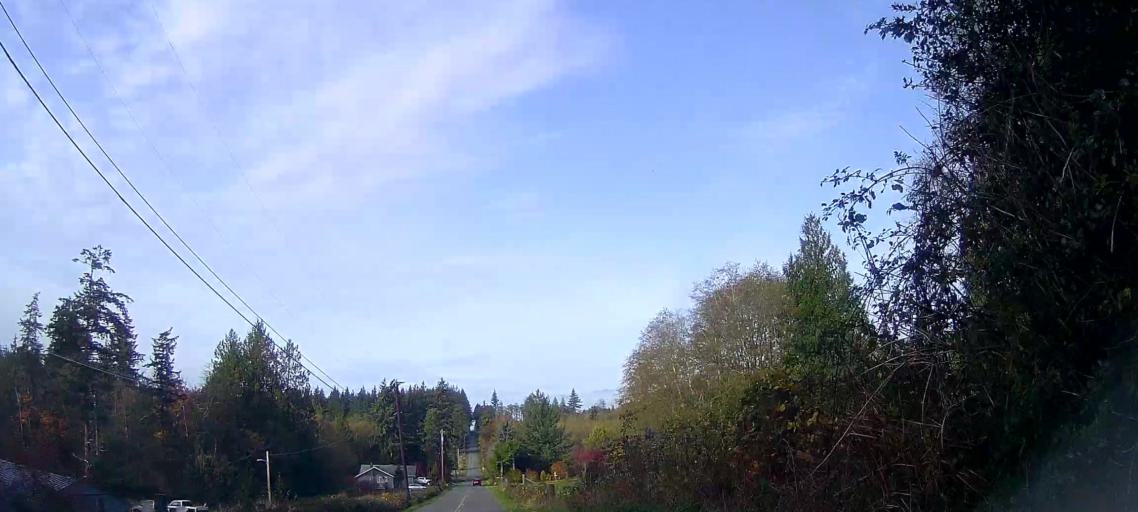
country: US
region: Washington
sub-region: Snohomish County
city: Stanwood
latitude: 48.2566
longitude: -122.3414
